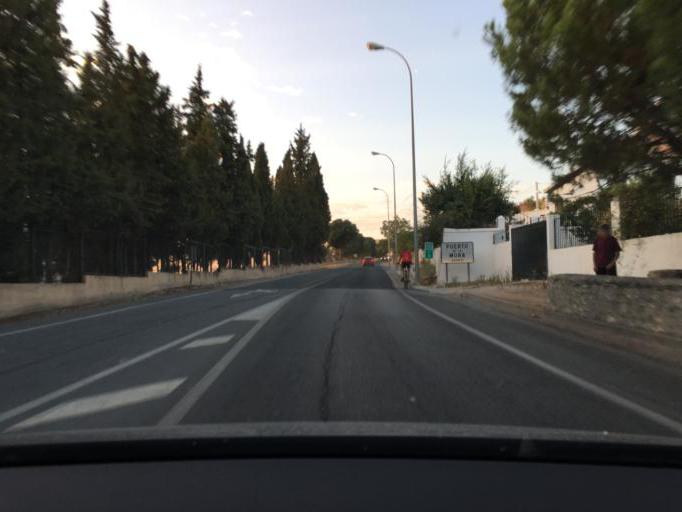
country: ES
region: Andalusia
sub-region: Provincia de Granada
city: Granada
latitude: 37.1909
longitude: -3.5926
